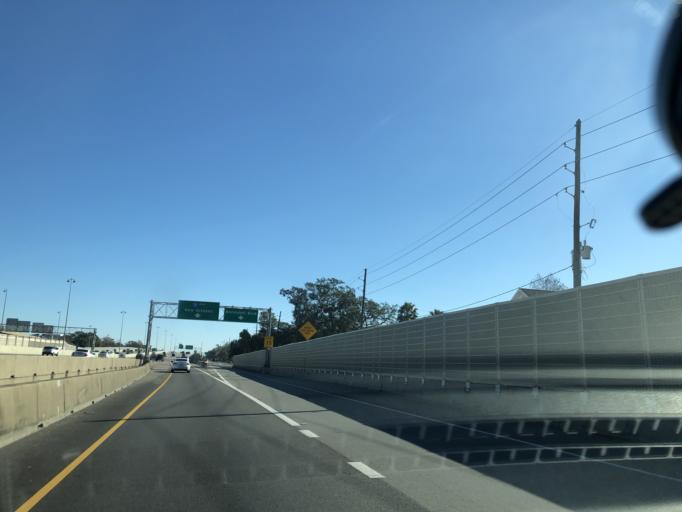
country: US
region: Louisiana
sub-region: Jefferson Parish
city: Metairie
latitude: 29.9968
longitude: -90.1494
